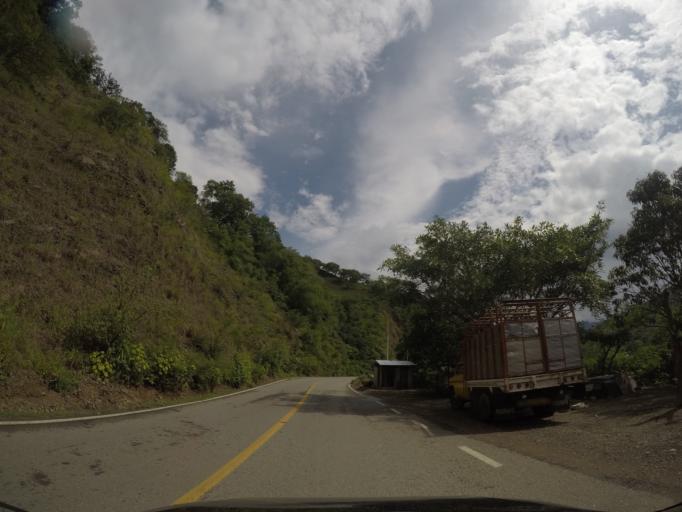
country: MX
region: Oaxaca
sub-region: San Jeronimo Coatlan
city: San Cristobal Honduras
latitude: 16.3789
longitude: -97.0767
